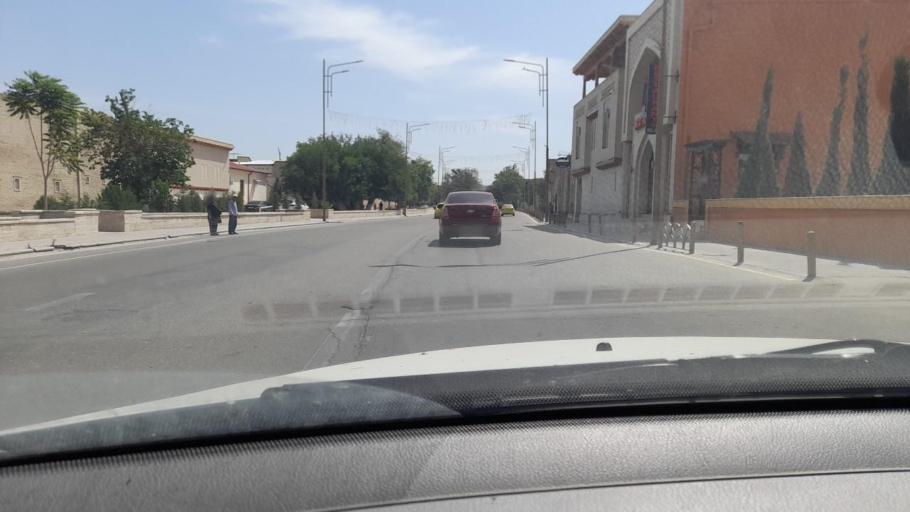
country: UZ
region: Bukhara
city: Bukhara
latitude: 39.7732
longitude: 64.4245
